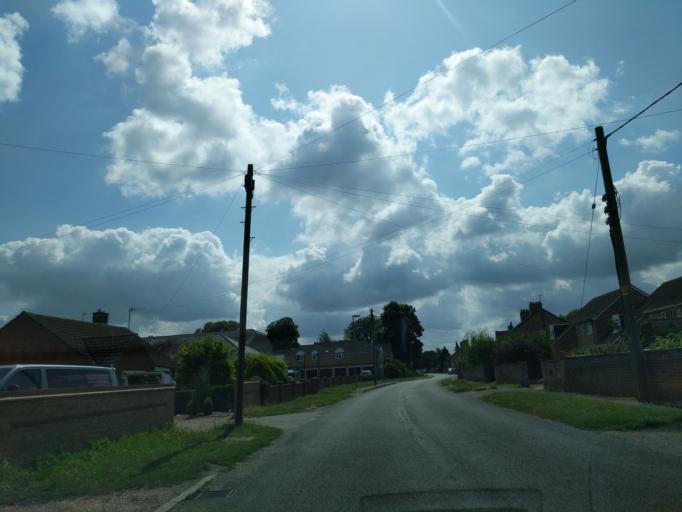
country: GB
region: England
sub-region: Cambridgeshire
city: Isleham
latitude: 52.3148
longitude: 0.3814
